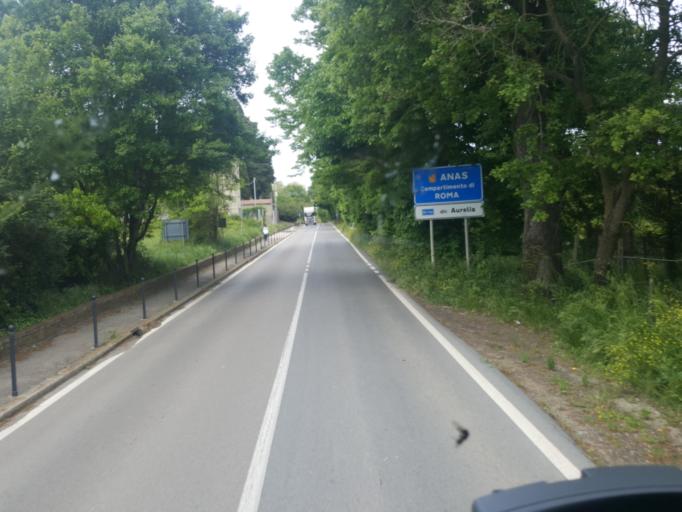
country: IT
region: Latium
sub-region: Provincia di Viterbo
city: Monte Romano
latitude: 42.2727
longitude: 11.9066
